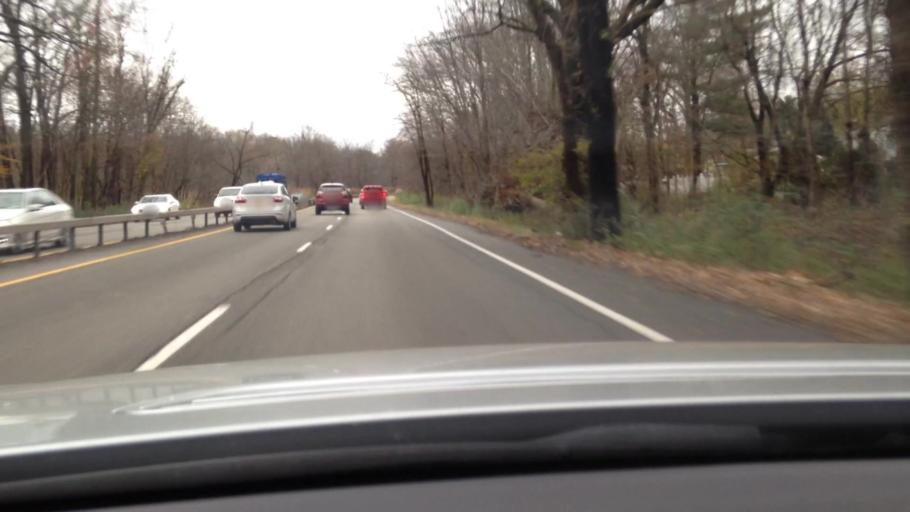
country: US
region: New York
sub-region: Westchester County
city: Briarcliff Manor
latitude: 41.1616
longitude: -73.8370
